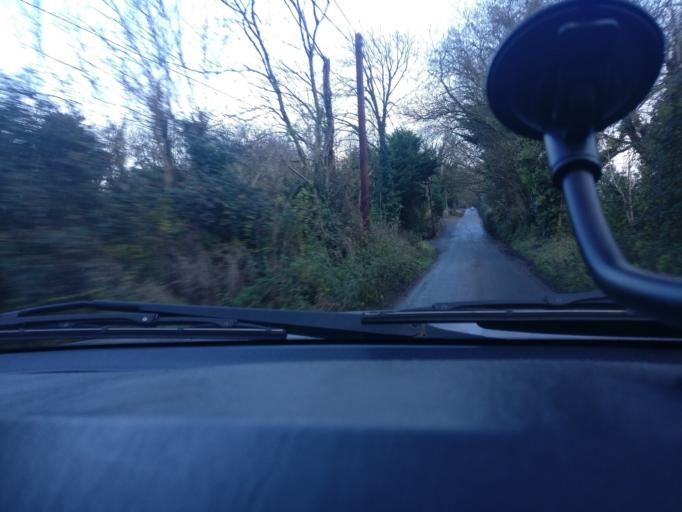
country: IE
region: Connaught
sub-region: County Galway
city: Athenry
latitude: 53.1988
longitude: -8.7046
